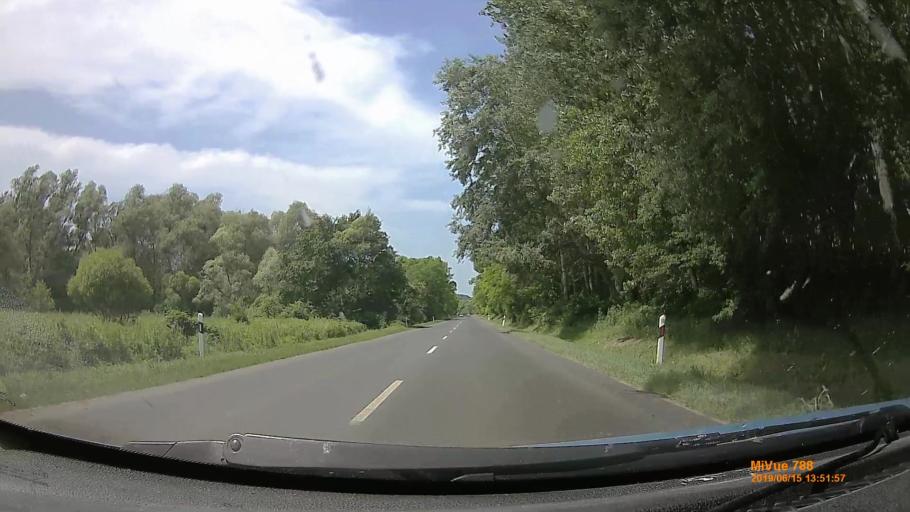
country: HU
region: Tolna
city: Iregszemcse
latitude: 46.7602
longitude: 18.1582
